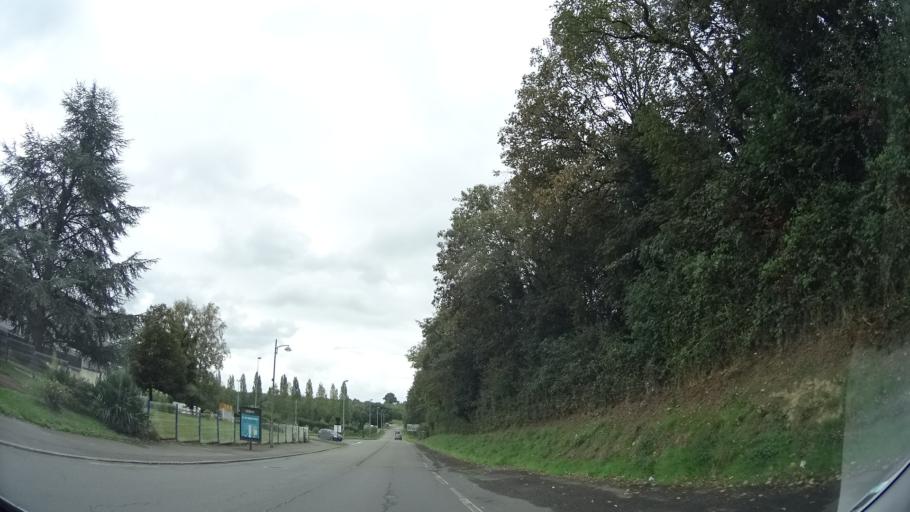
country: FR
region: Brittany
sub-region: Departement d'Ille-et-Vilaine
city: Chasne-sur-Illet
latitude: 48.2598
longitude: -1.6060
